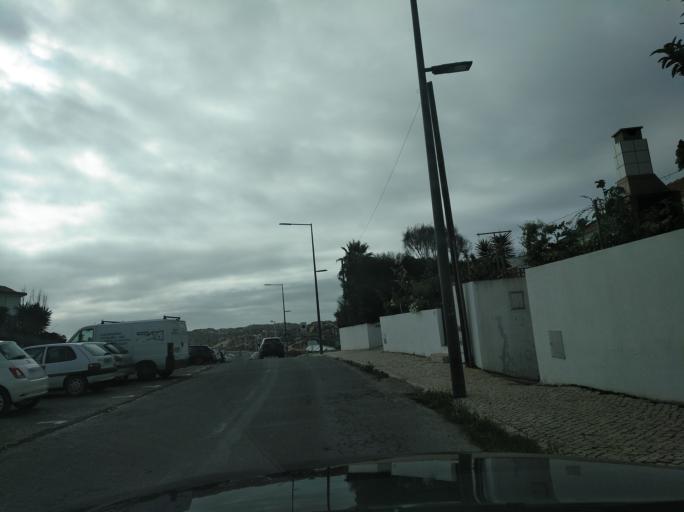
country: PT
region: Beja
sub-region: Odemira
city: Vila Nova de Milfontes
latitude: 37.7235
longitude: -8.7859
